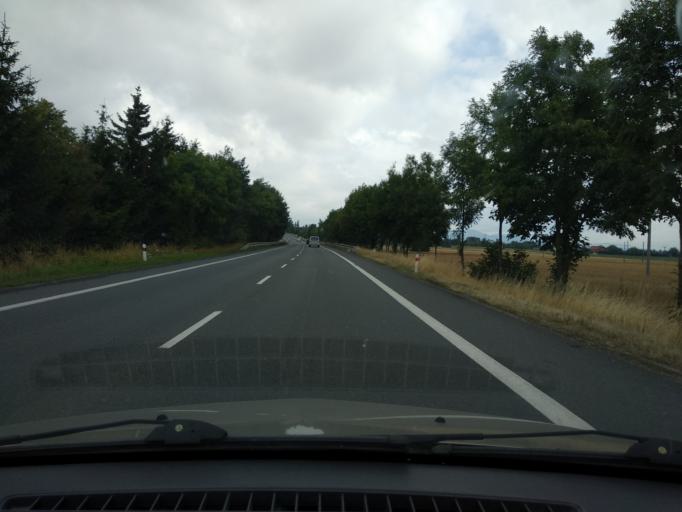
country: CZ
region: Olomoucky
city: Zabreh
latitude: 49.8818
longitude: 16.8933
